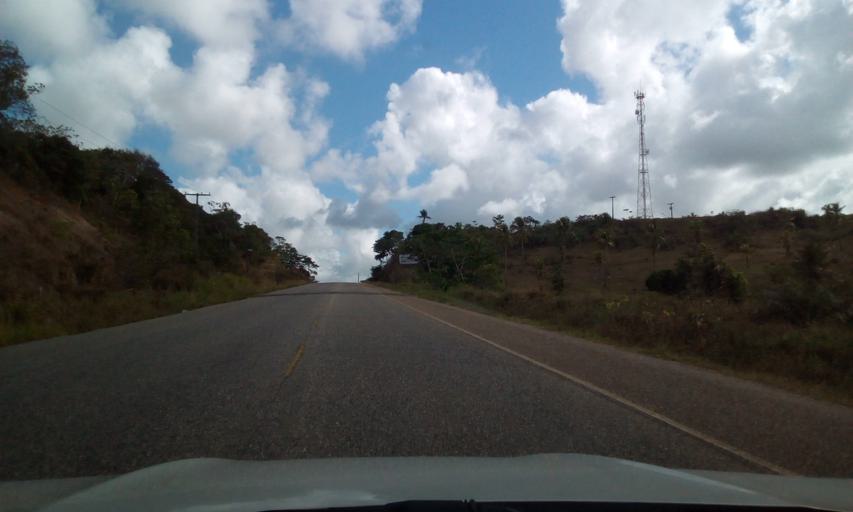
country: BR
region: Sergipe
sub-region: Estancia
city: Estancia
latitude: -11.3599
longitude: -37.4536
